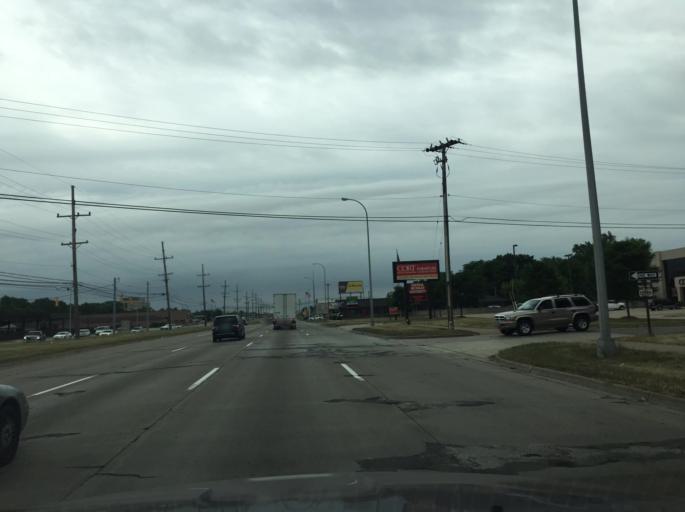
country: US
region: Michigan
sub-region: Macomb County
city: Center Line
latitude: 42.5019
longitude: -83.0466
